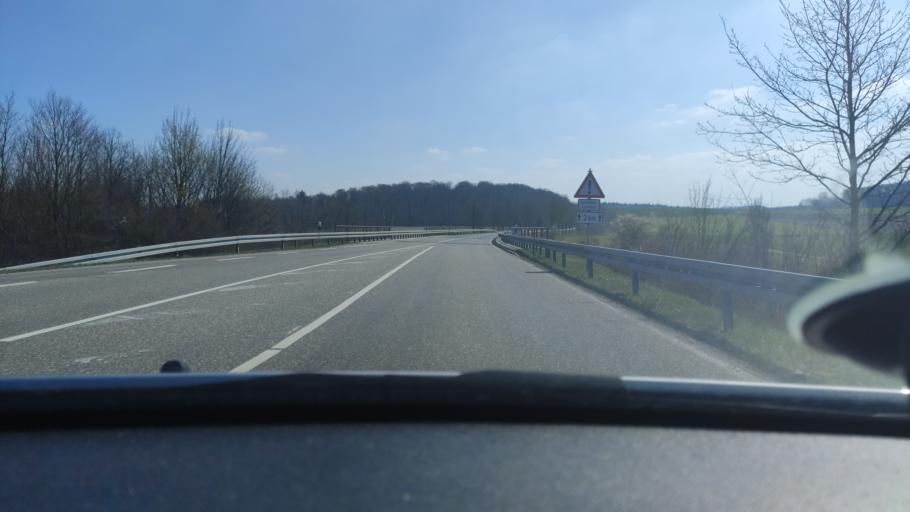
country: DE
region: Baden-Wuerttemberg
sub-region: Regierungsbezirk Stuttgart
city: Boxberg
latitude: 49.4533
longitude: 9.6601
